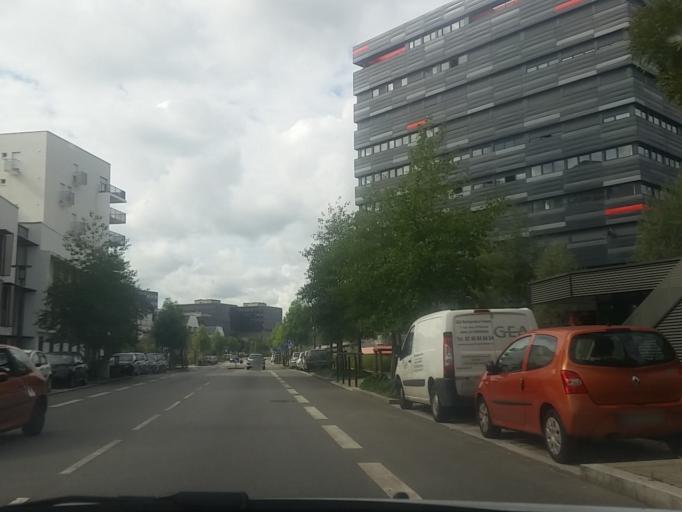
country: FR
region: Pays de la Loire
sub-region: Departement de la Loire-Atlantique
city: Saint-Sebastien-sur-Loire
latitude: 47.2104
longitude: -1.5287
